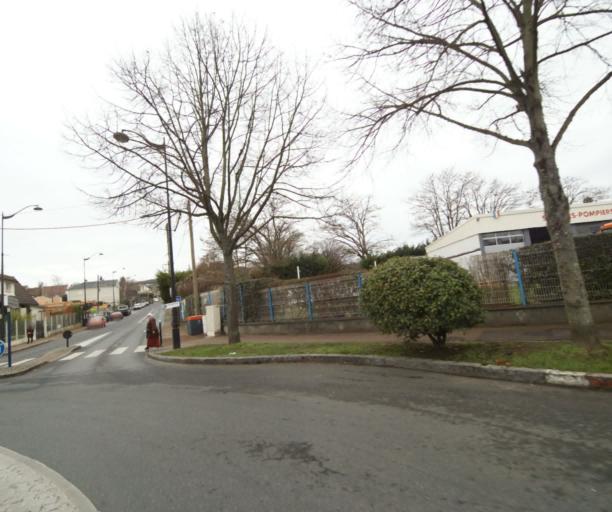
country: FR
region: Ile-de-France
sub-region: Departement des Hauts-de-Seine
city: Rueil-Malmaison
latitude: 48.8648
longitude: 2.1793
